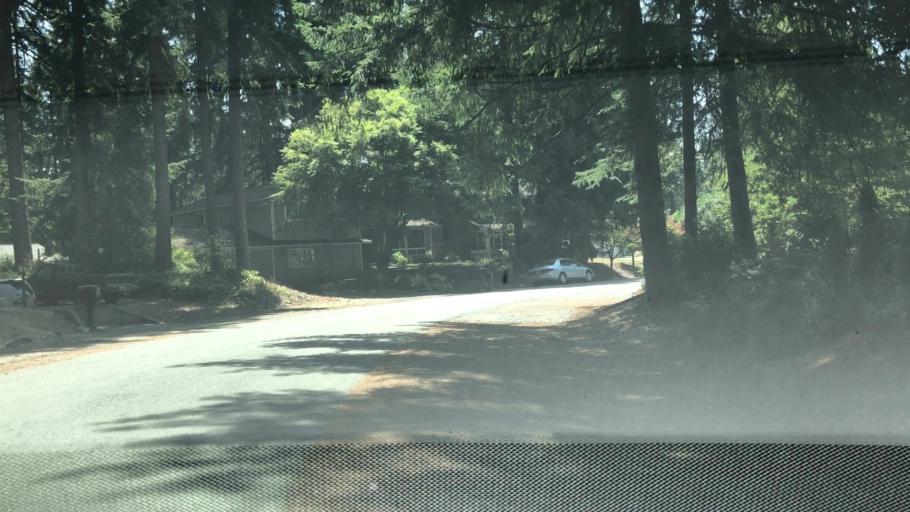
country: US
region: Washington
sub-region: King County
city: Cottage Lake
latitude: 47.7502
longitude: -122.0853
